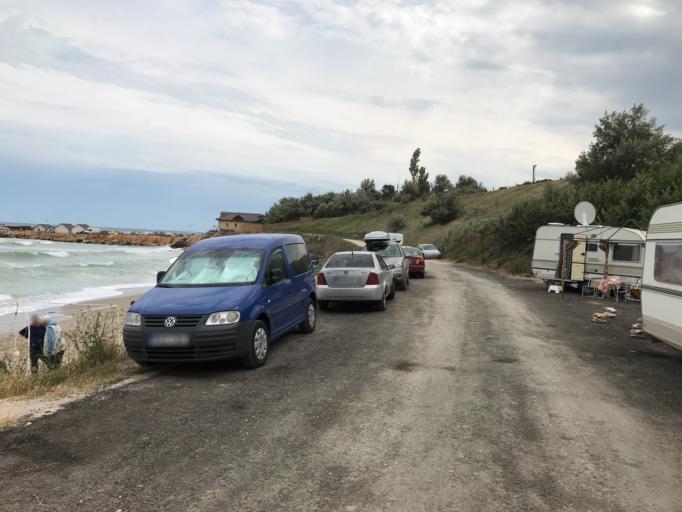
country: RO
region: Constanta
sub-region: Municipiul Mangalia
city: Mangalia
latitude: 43.7815
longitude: 28.5797
